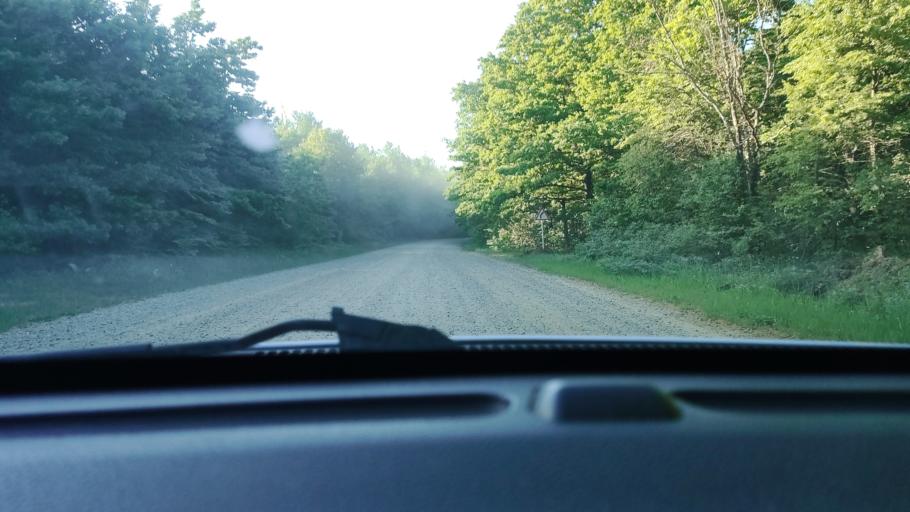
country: RU
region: Krasnodarskiy
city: Goryachiy Klyuch
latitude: 44.7123
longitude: 38.9916
